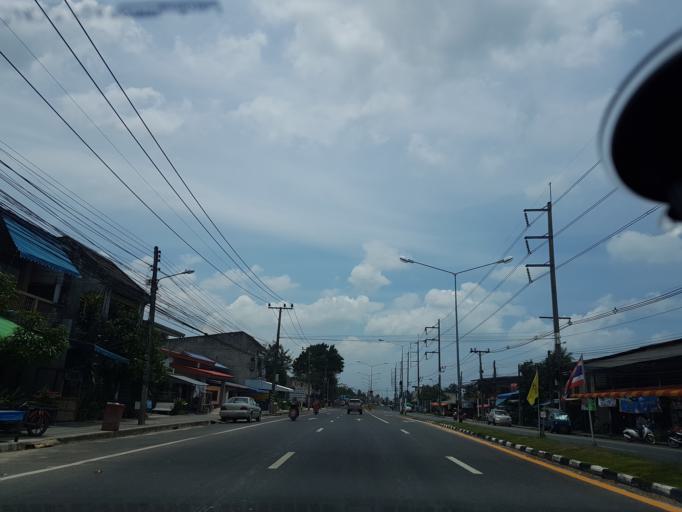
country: TH
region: Songkhla
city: Songkhla
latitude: 7.1052
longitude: 100.6331
